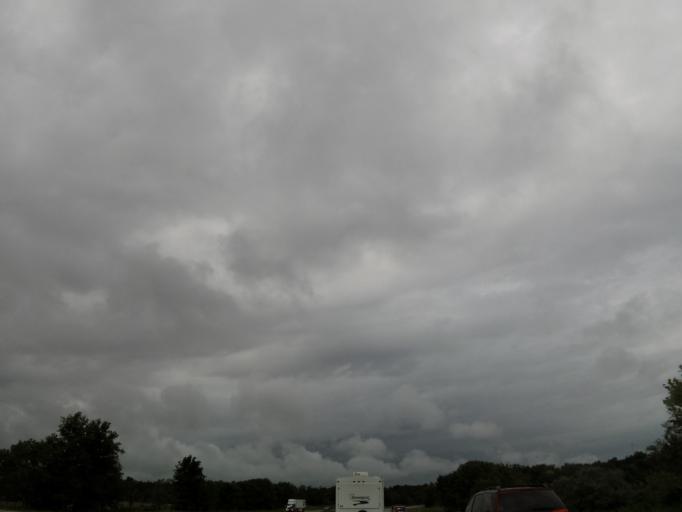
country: US
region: Illinois
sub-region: Clinton County
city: Wamac
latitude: 38.3625
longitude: -89.0783
